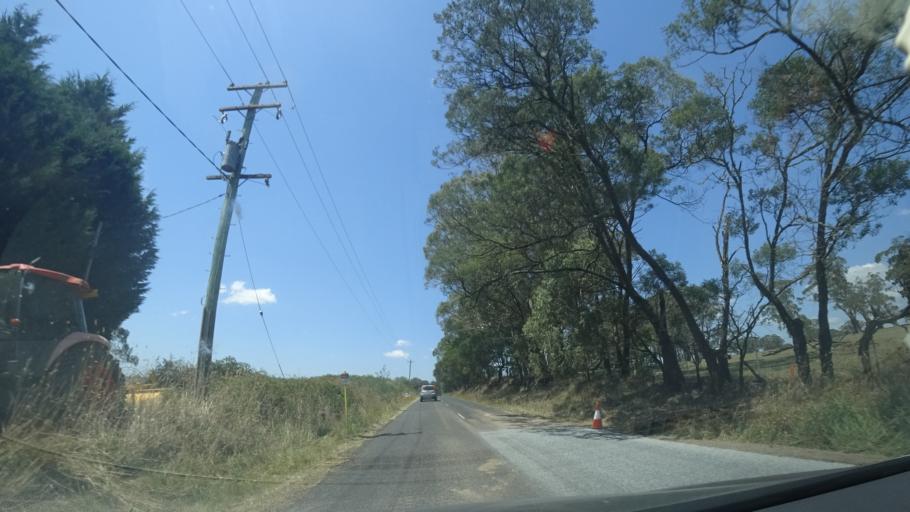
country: AU
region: New South Wales
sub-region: Wingecarribee
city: Bundanoon
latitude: -34.6104
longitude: 150.2664
